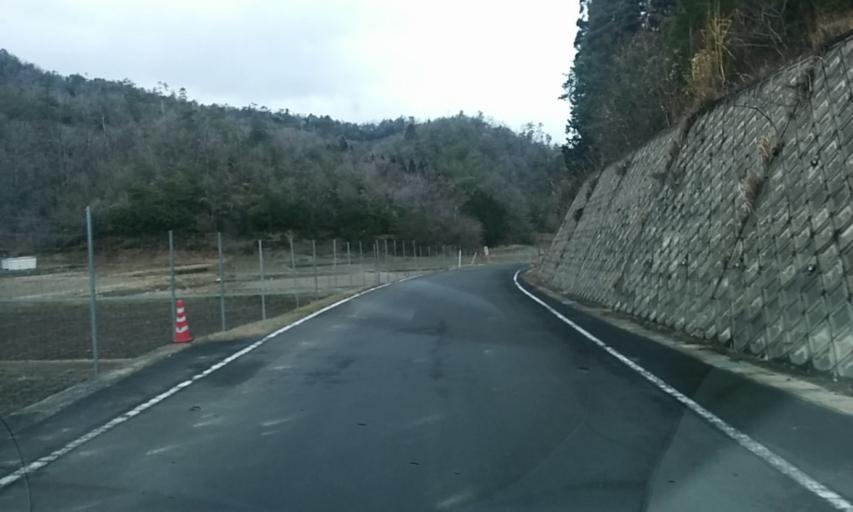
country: JP
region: Kyoto
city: Kameoka
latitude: 35.1152
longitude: 135.4235
